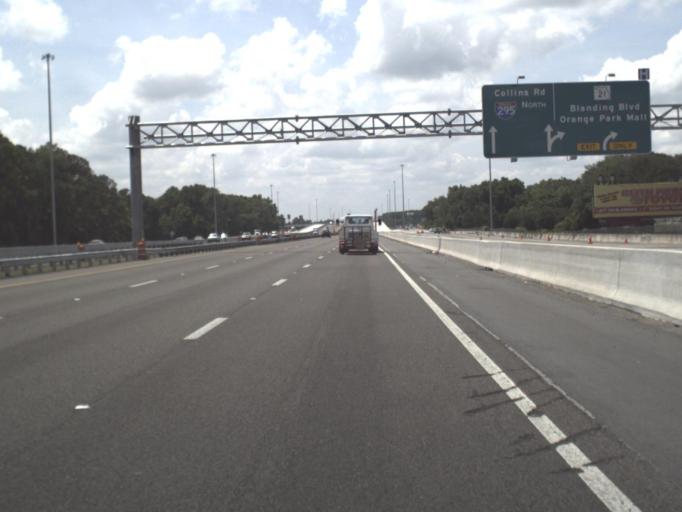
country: US
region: Florida
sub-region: Clay County
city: Bellair-Meadowbrook Terrace
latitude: 30.1928
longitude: -81.7288
